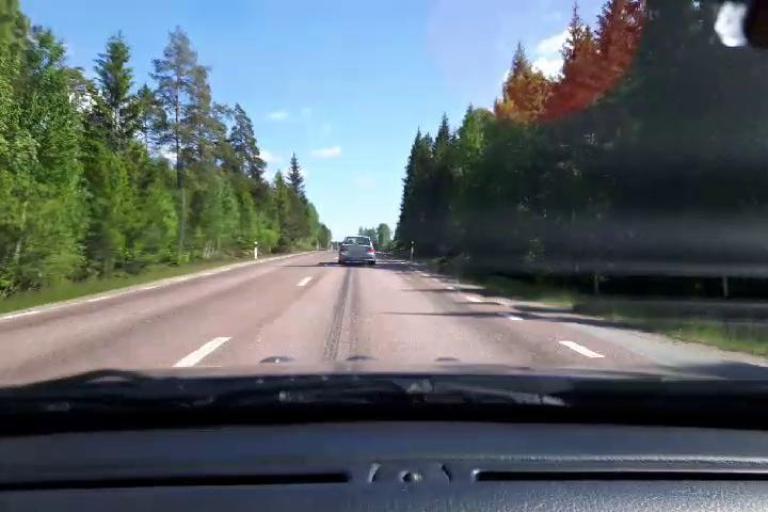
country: SE
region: Gaevleborg
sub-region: Hudiksvalls Kommun
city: Sorforsa
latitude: 61.7514
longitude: 16.8303
